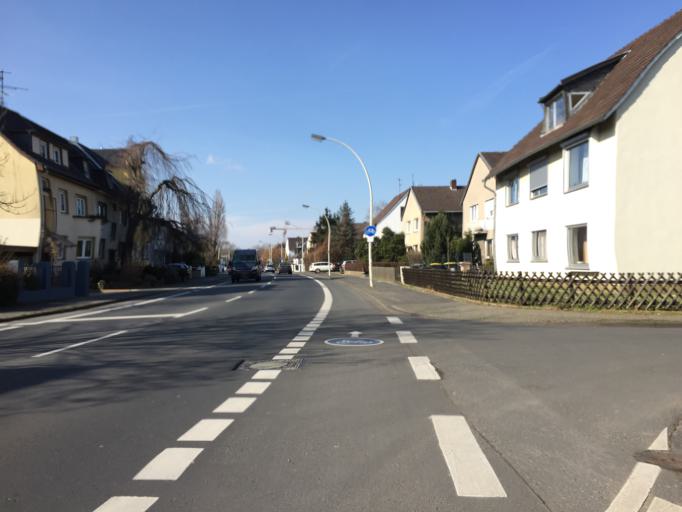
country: DE
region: North Rhine-Westphalia
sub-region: Regierungsbezirk Koln
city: Bonn
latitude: 50.7314
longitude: 7.0698
